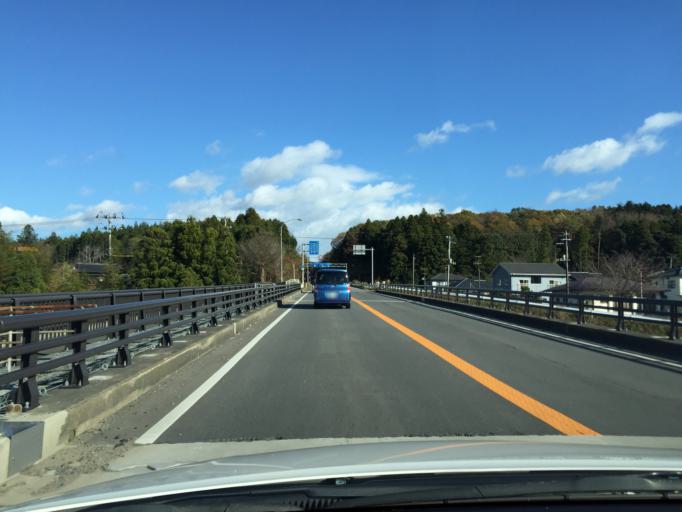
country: JP
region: Fukushima
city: Namie
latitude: 37.2897
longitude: 140.9919
